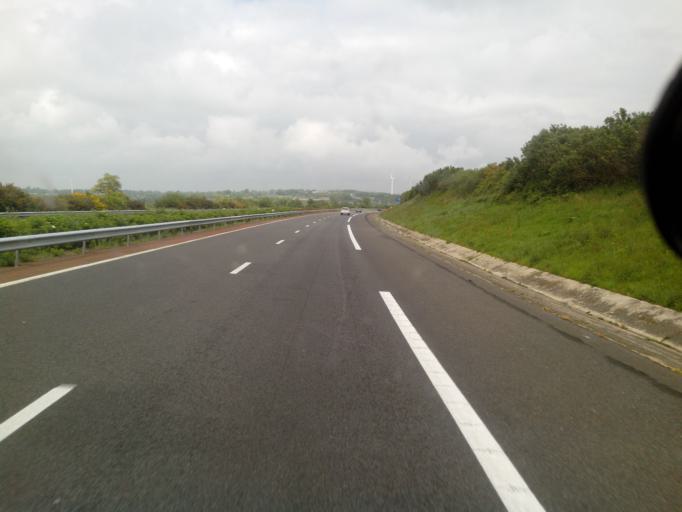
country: FR
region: Lower Normandy
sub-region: Departement de la Manche
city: Percy
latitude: 48.8920
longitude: -1.1313
